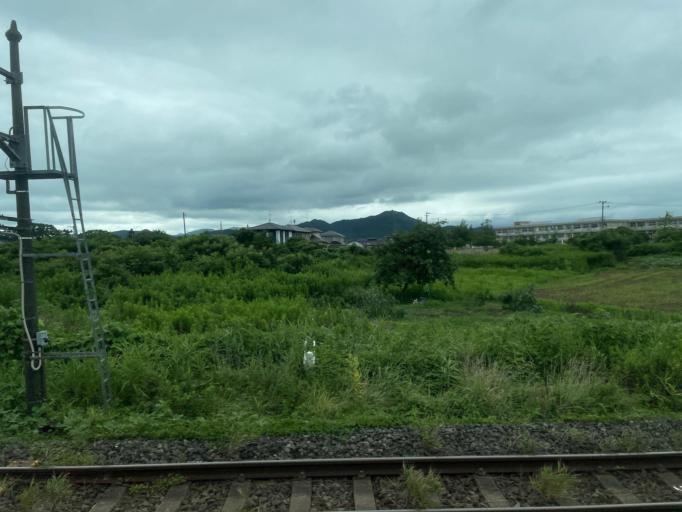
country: JP
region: Fukushima
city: Motomiya
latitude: 37.4935
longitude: 140.3952
